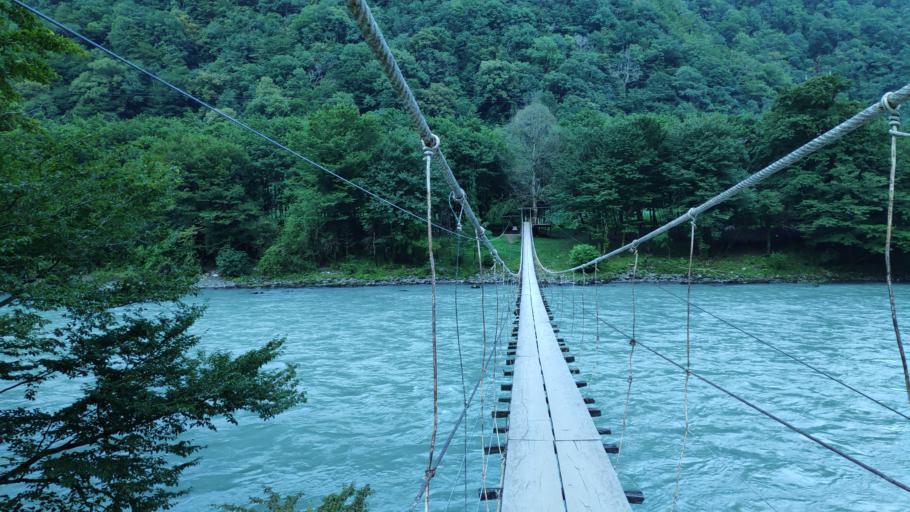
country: GE
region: Abkhazia
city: Bich'vinta
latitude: 43.2609
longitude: 40.3953
